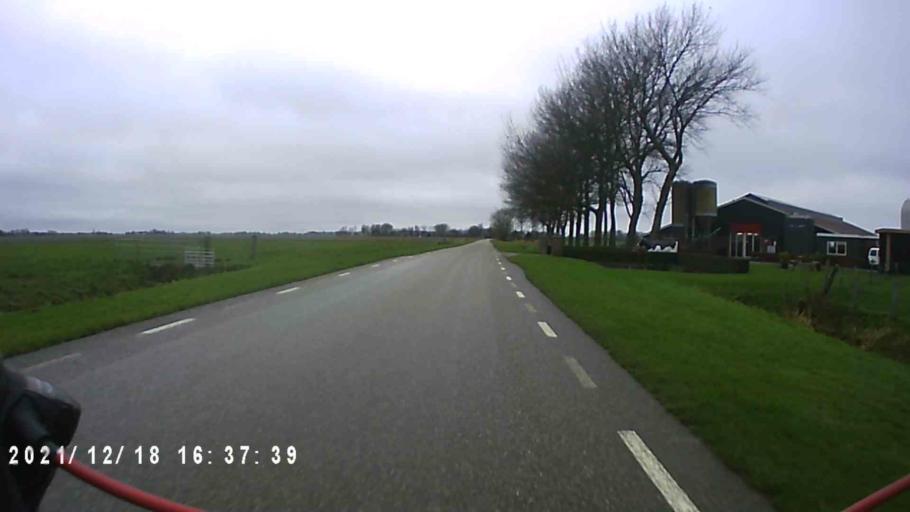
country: NL
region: Friesland
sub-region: Gemeente Dongeradeel
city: Dokkum
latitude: 53.3578
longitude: 6.0147
